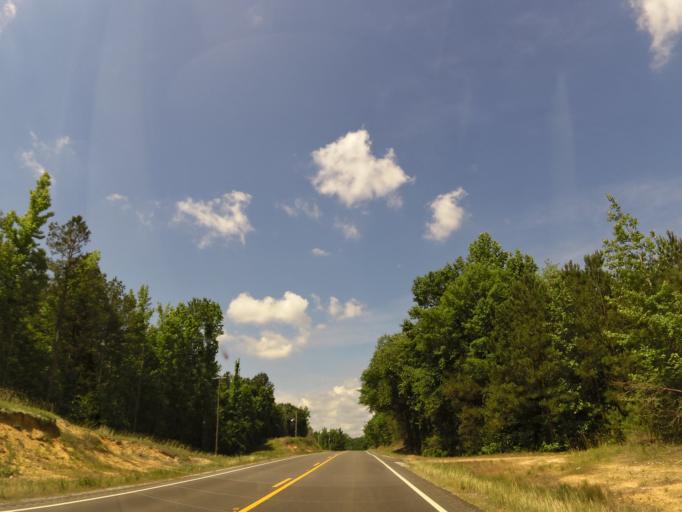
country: US
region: Alabama
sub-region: Marion County
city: Guin
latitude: 33.9386
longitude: -88.0018
